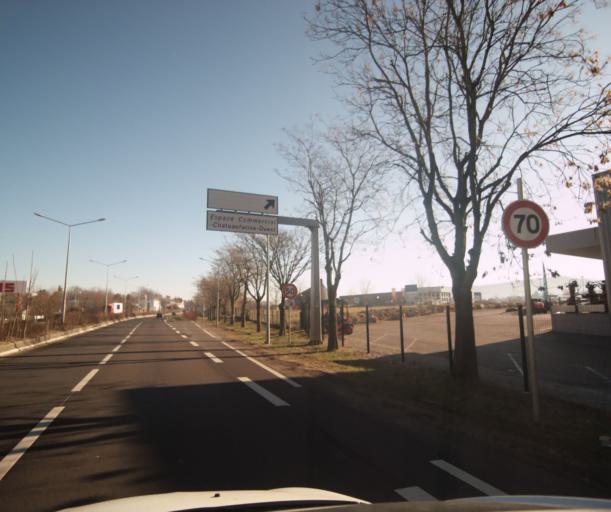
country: FR
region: Franche-Comte
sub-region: Departement du Doubs
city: Franois
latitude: 47.2174
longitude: 5.9432
